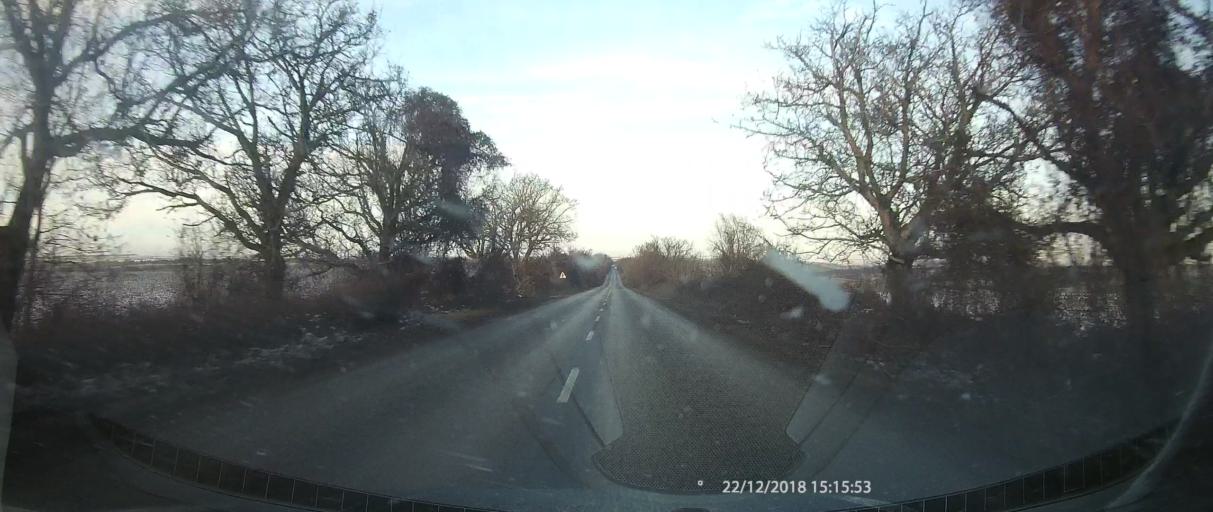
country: BG
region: Ruse
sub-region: Obshtina Dve Mogili
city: Dve Mogili
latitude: 43.5978
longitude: 25.8401
